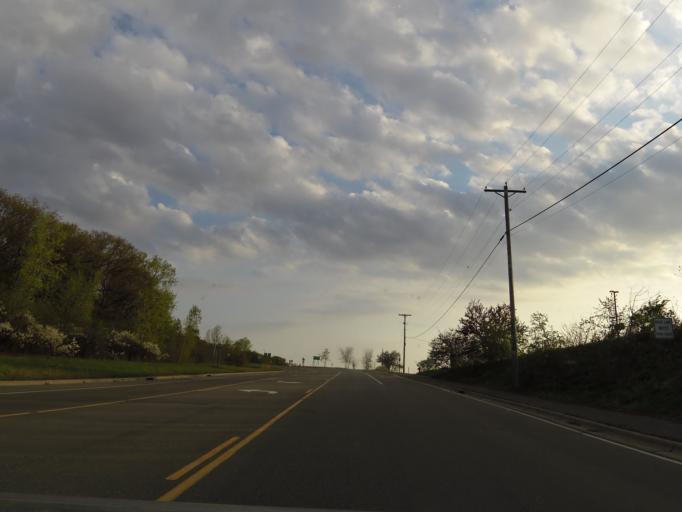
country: US
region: Minnesota
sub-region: Dakota County
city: Mendota Heights
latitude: 44.8855
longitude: -93.1677
